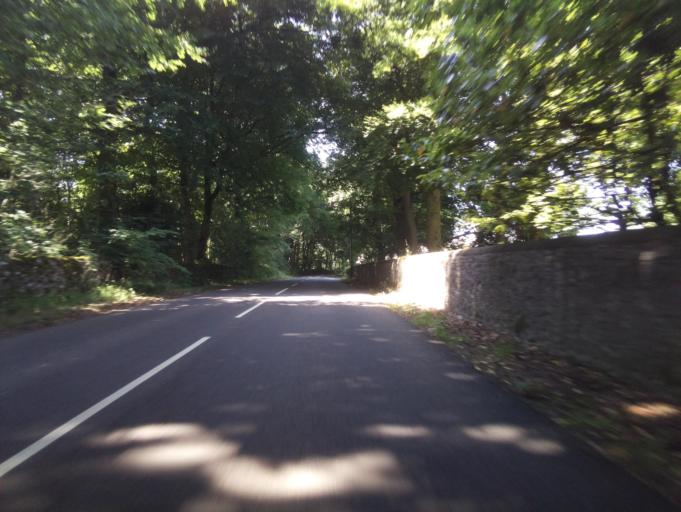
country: GB
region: England
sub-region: Derbyshire
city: Tideswell
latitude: 53.2722
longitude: -1.8215
